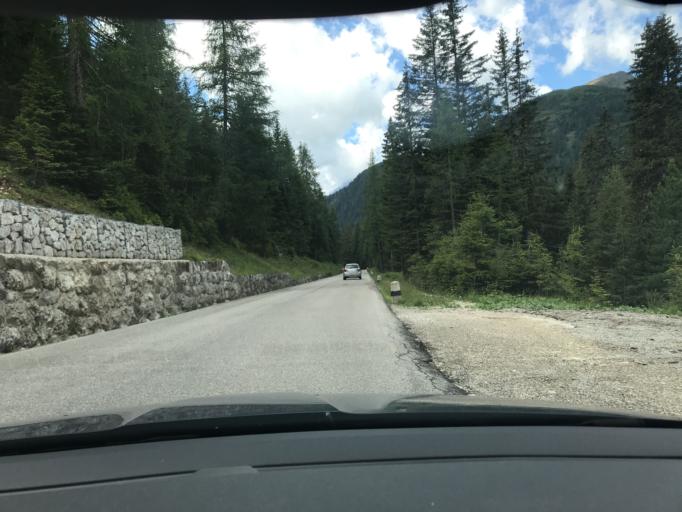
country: IT
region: Veneto
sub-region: Provincia di Belluno
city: Livinallongo del Col di Lana
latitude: 46.5050
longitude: 11.9973
